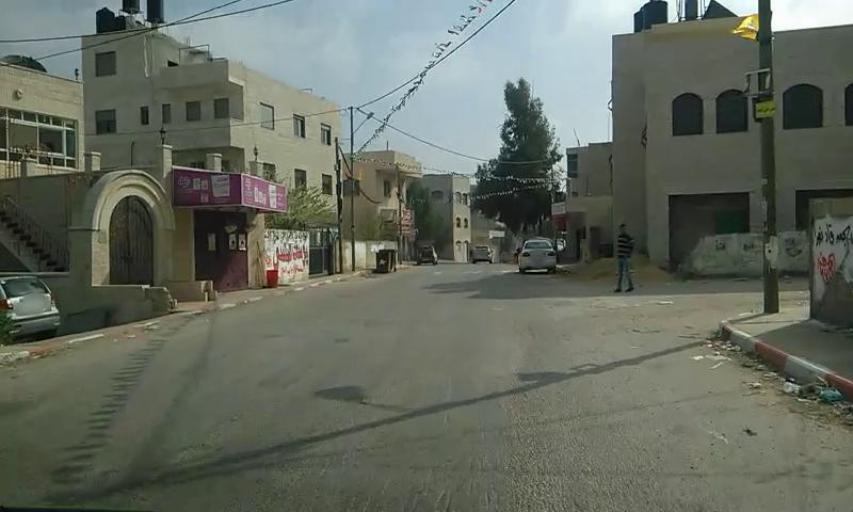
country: PS
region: West Bank
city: Dura al Qar`
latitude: 31.9580
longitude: 35.2265
